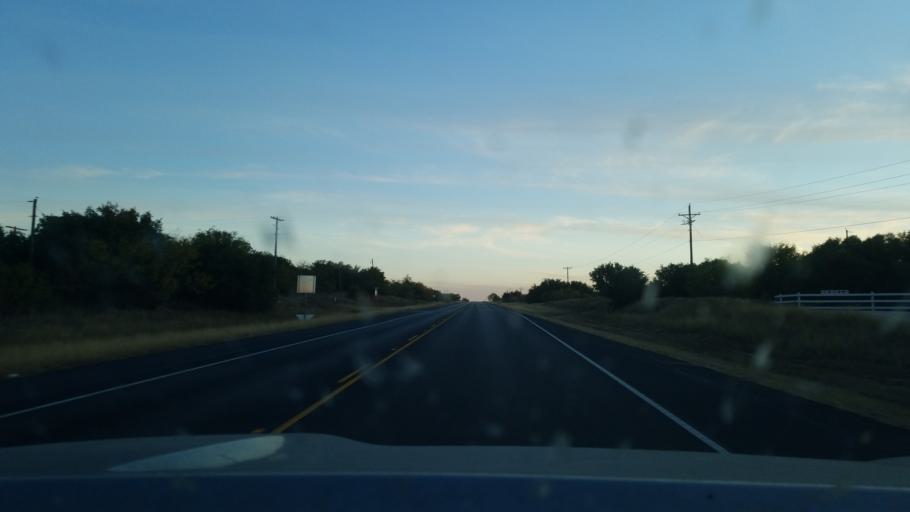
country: US
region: Texas
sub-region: Stephens County
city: Breckenridge
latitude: 32.6891
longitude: -98.9026
